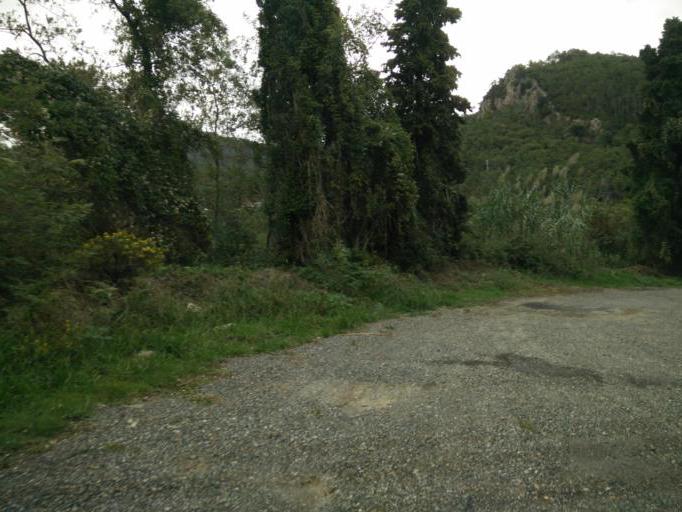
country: IT
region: Liguria
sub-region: Provincia di La Spezia
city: Framura
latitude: 44.2150
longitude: 9.5596
